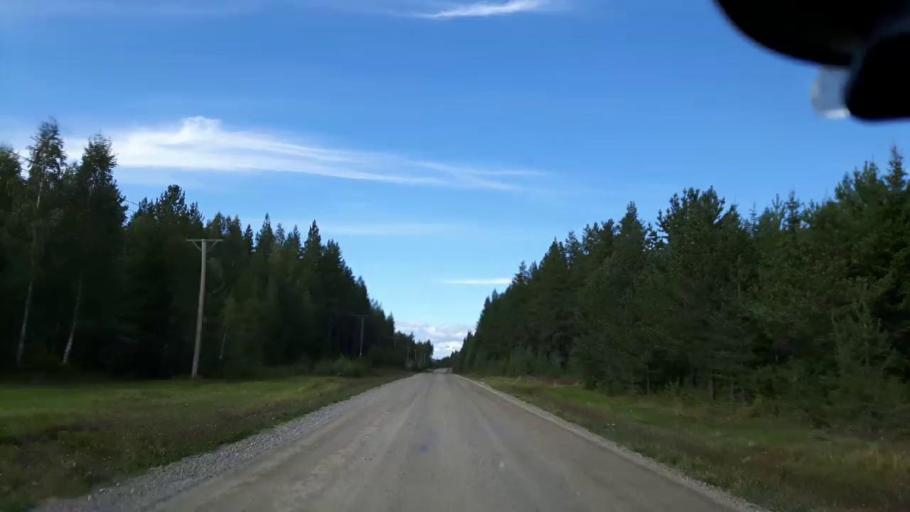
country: SE
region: Jaemtland
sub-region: Ragunda Kommun
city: Hammarstrand
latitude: 63.1385
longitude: 16.2373
